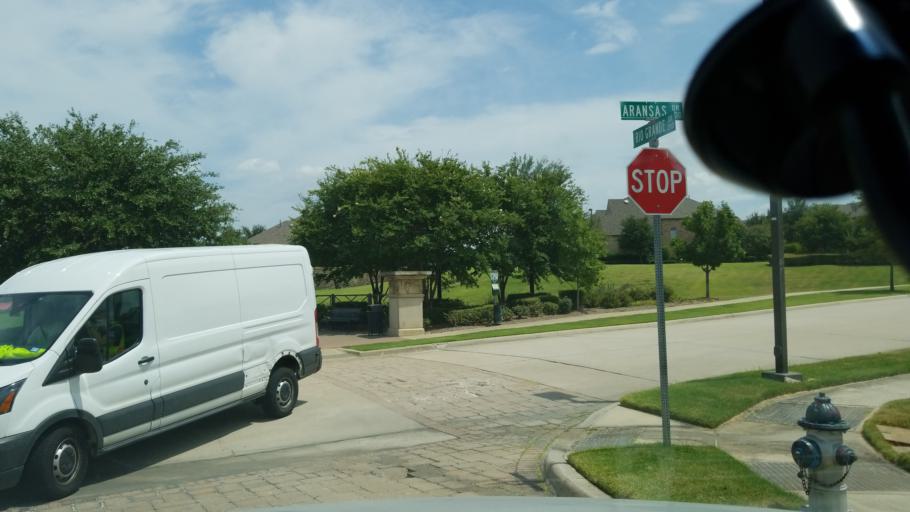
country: US
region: Texas
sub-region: Dallas County
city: Farmers Branch
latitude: 32.9050
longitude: -96.9467
